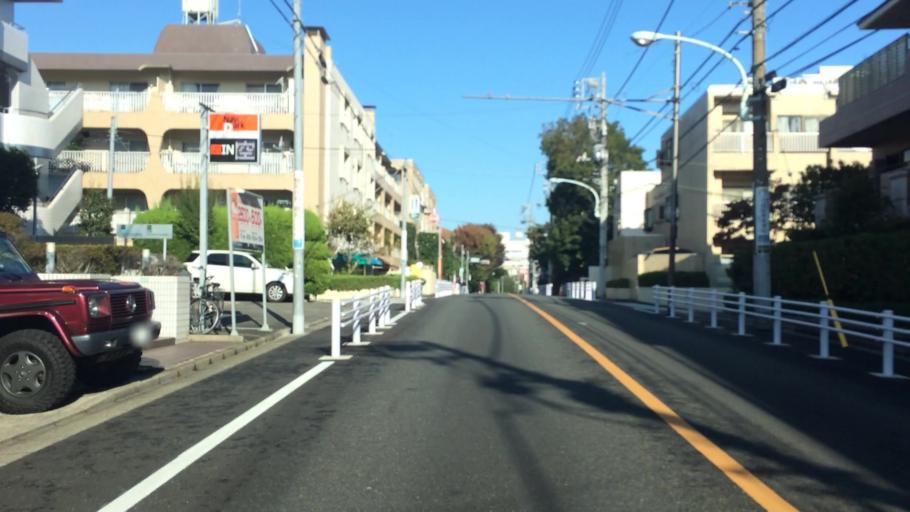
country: JP
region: Tokyo
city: Tokyo
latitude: 35.6194
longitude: 139.6676
